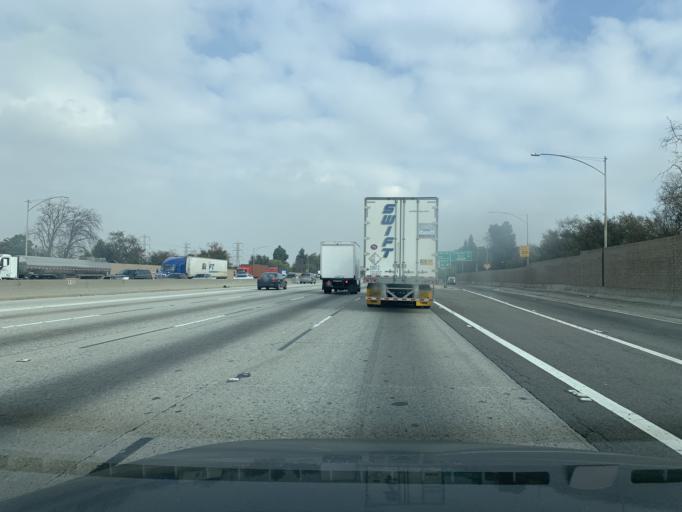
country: US
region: California
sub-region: Los Angeles County
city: Santa Fe Springs
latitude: 33.9462
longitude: -118.0938
